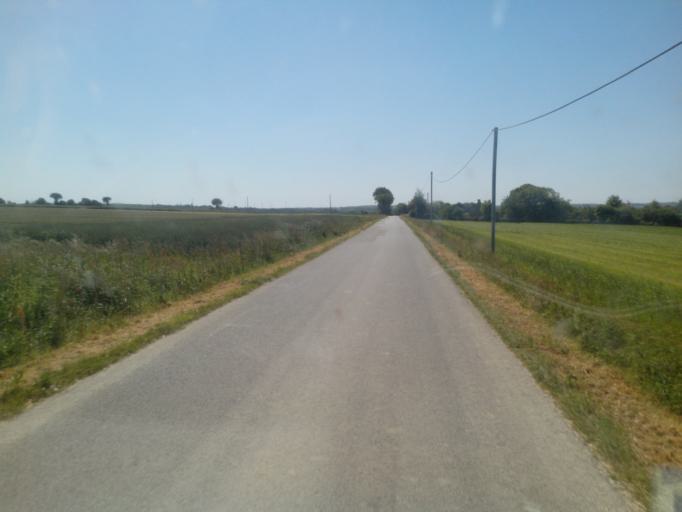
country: FR
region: Brittany
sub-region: Departement des Cotes-d'Armor
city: Merdrignac
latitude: 48.1420
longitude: -2.3607
